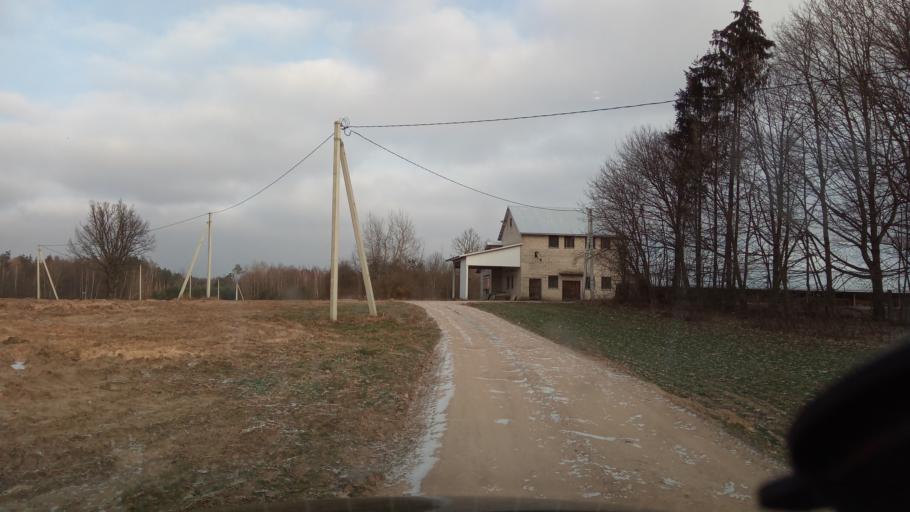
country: LT
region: Alytaus apskritis
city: Varena
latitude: 54.1257
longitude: 24.6601
